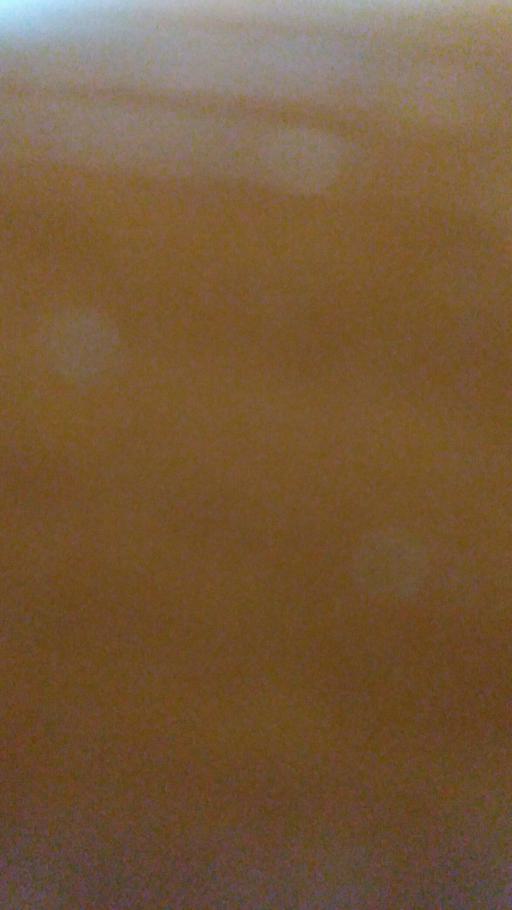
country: RU
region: Tula
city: Volovo
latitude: 53.5865
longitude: 38.1087
